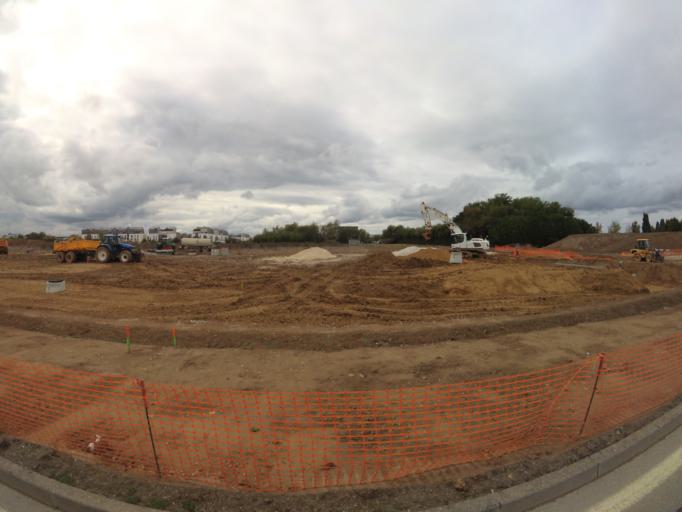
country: FR
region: Ile-de-France
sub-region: Departement de Seine-et-Marne
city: Montevrain
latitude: 48.8604
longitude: 2.7662
